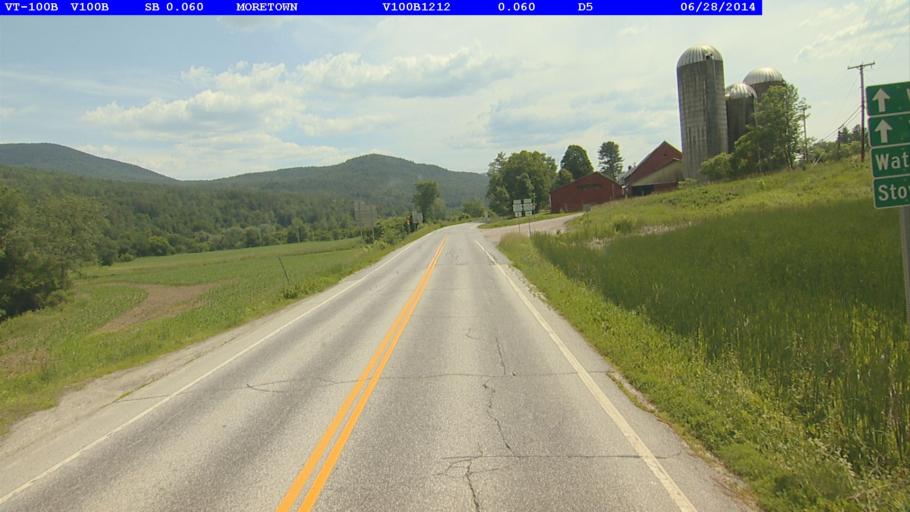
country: US
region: Vermont
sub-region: Washington County
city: Waterbury
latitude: 44.2411
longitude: -72.7755
